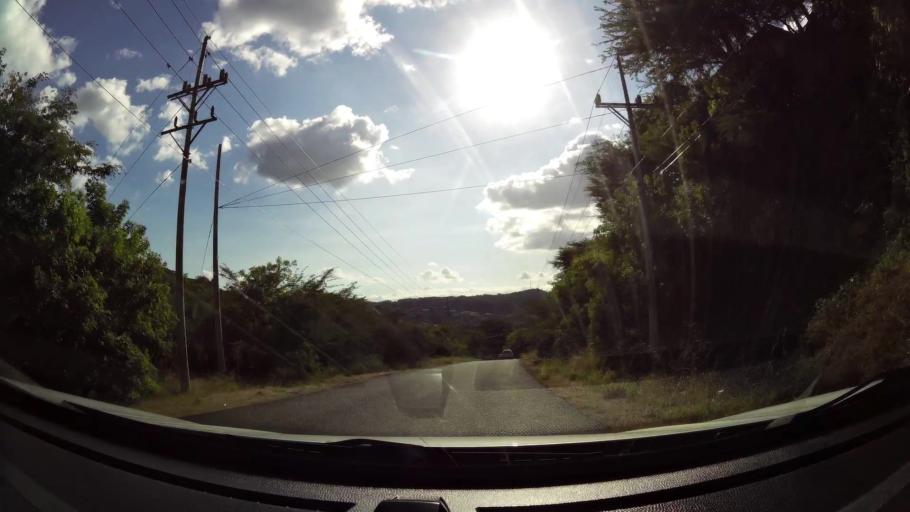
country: CR
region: Guanacaste
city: Sardinal
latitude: 10.5792
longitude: -85.6699
